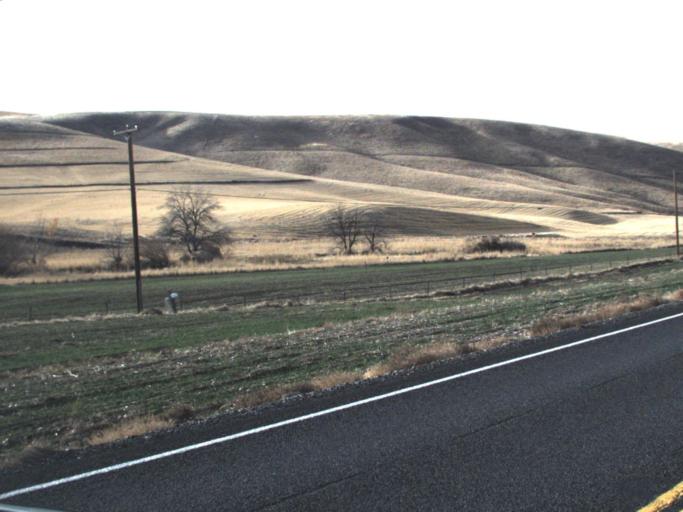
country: US
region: Washington
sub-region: Garfield County
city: Pomeroy
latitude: 46.4732
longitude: -117.7235
